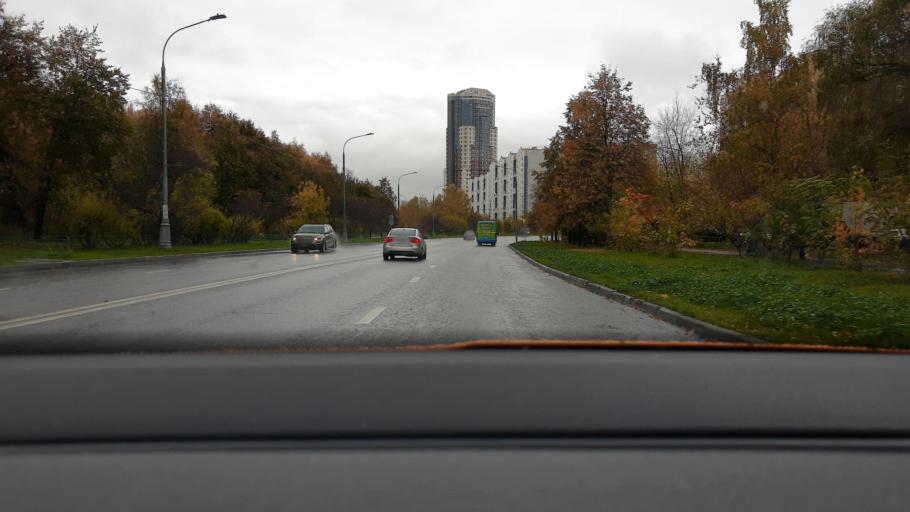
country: RU
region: Moscow
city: Strogino
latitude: 55.8098
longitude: 37.4154
